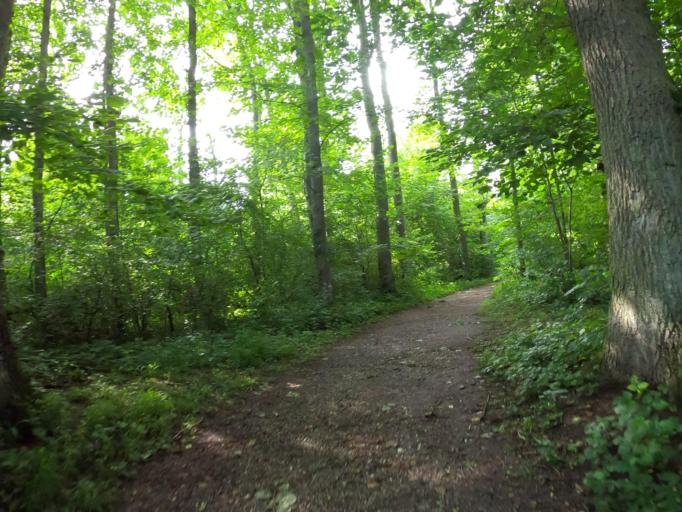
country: DE
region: Bavaria
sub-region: Swabia
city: Nersingen
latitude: 48.4456
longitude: 10.1552
